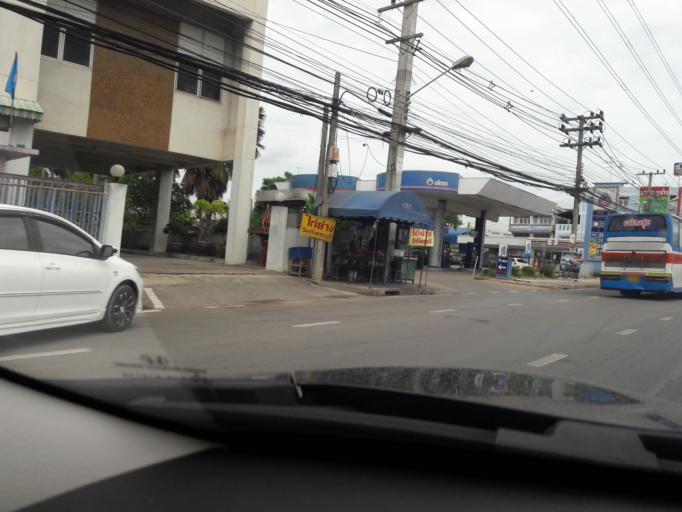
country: TH
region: Ratchaburi
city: Damnoen Saduak
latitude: 13.5318
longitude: 99.9670
